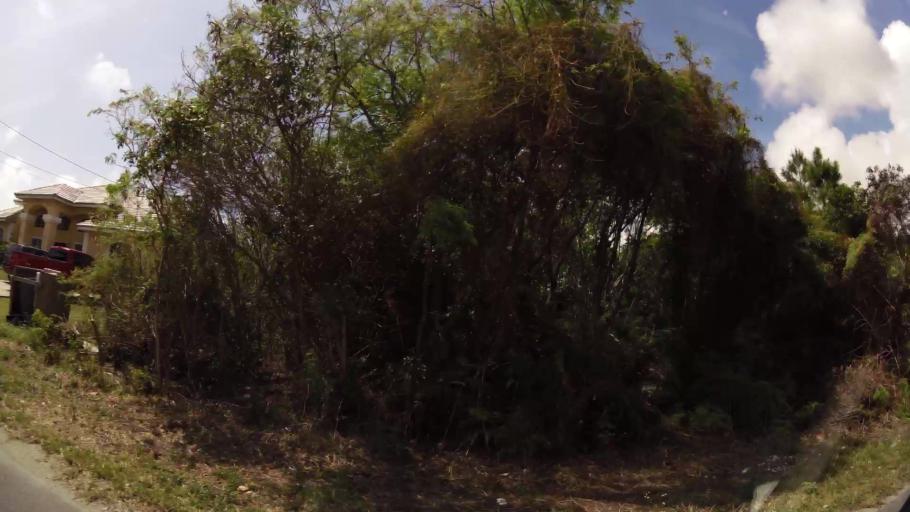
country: BS
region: Freeport
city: Freeport
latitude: 26.5097
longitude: -78.7255
